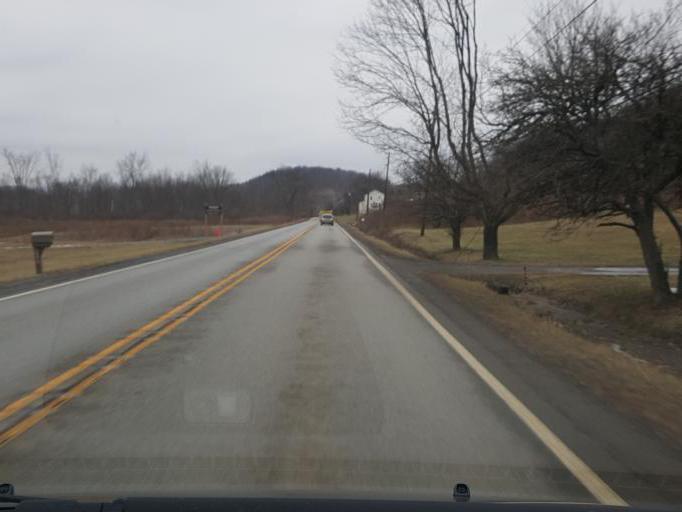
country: US
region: Pennsylvania
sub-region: Blair County
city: Greenwood
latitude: 40.5615
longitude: -78.3568
